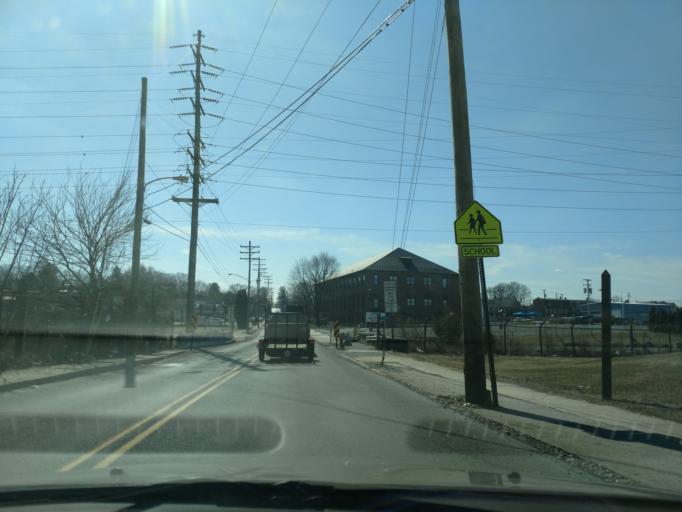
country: US
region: Pennsylvania
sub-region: Lebanon County
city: Lebanon
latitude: 40.3421
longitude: -76.4115
